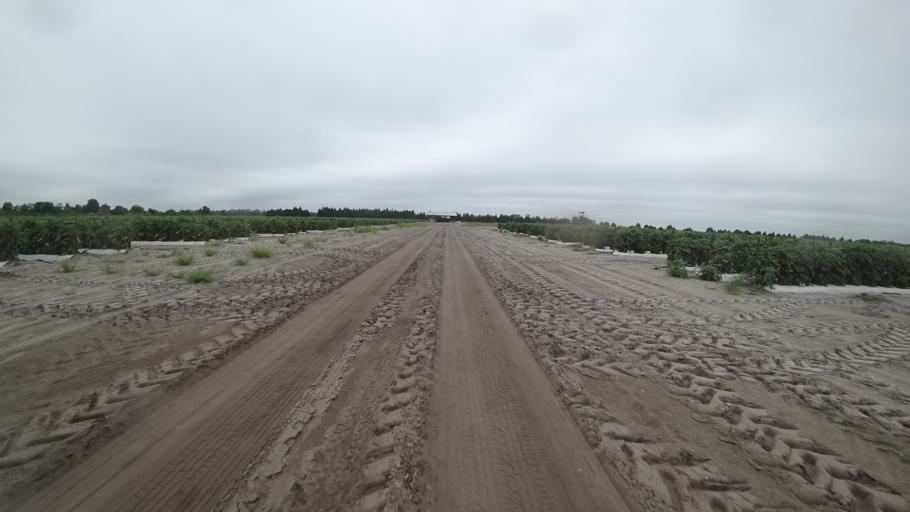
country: US
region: Florida
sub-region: DeSoto County
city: Arcadia
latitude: 27.3012
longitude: -82.1090
